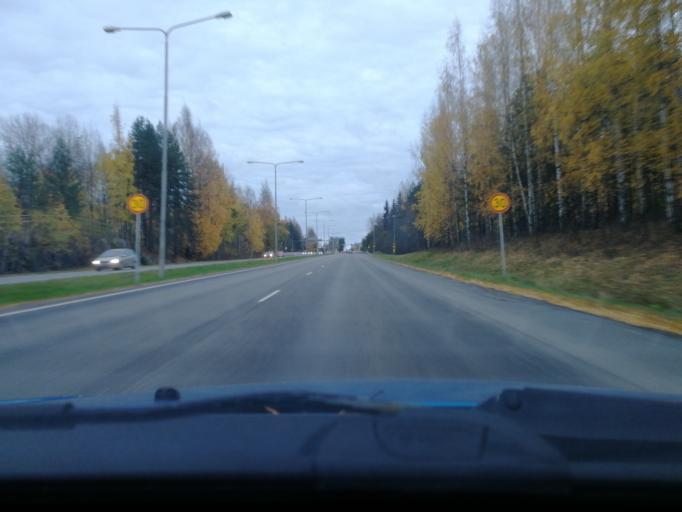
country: FI
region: Pirkanmaa
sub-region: Tampere
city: Tampere
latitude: 61.4690
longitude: 23.8408
